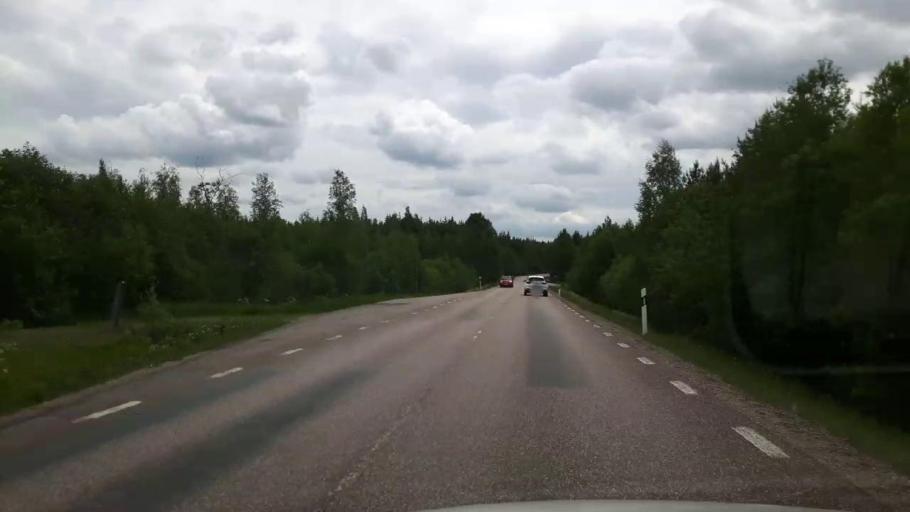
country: SE
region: Vaestmanland
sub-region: Norbergs Kommun
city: Norberg
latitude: 60.1246
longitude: 15.9182
